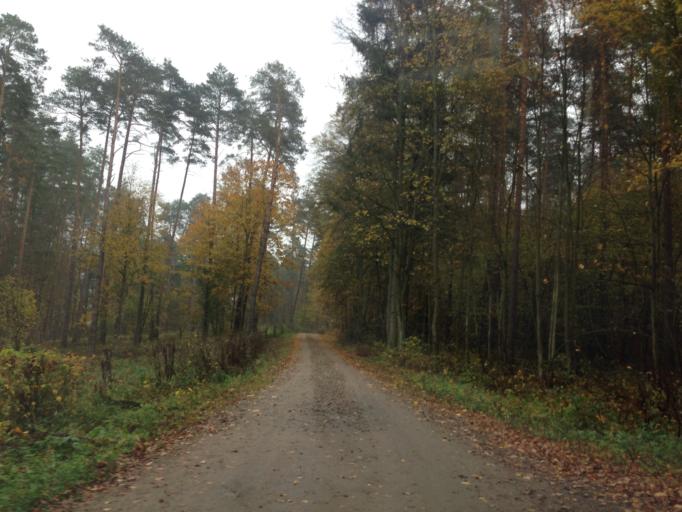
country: PL
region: Kujawsko-Pomorskie
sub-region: Powiat brodnicki
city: Gorzno
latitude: 53.2238
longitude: 19.6685
